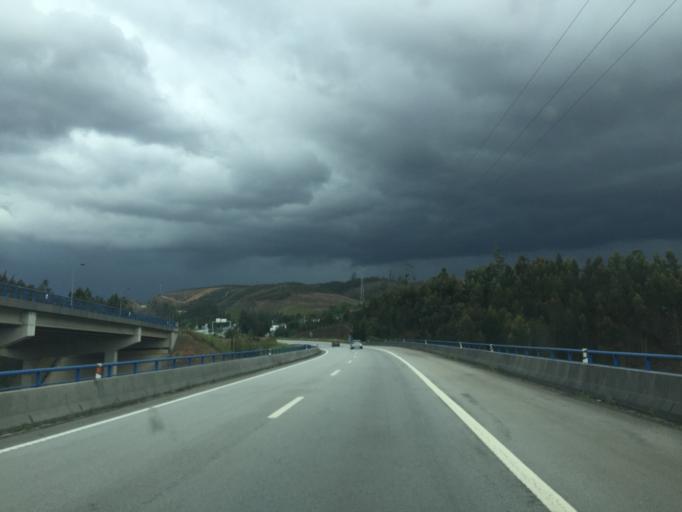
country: PT
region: Aveiro
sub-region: Albergaria-A-Velha
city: Albergaria-a-Velha
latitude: 40.6771
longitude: -8.4465
